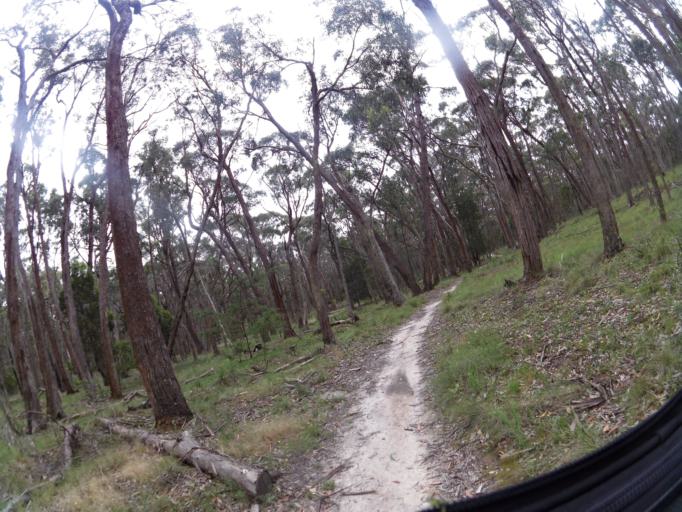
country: AU
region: Victoria
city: Brown Hill
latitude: -37.4623
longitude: 143.9066
